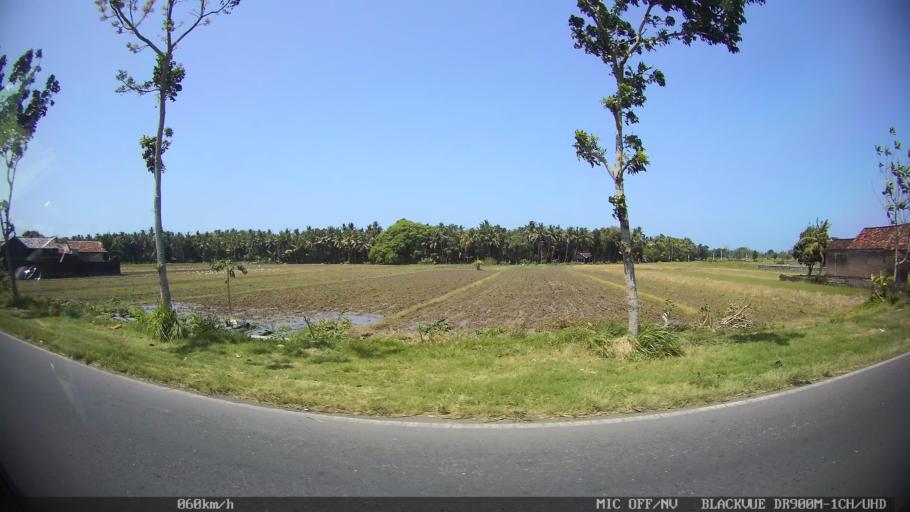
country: ID
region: Daerah Istimewa Yogyakarta
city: Srandakan
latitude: -7.9523
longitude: 110.2011
